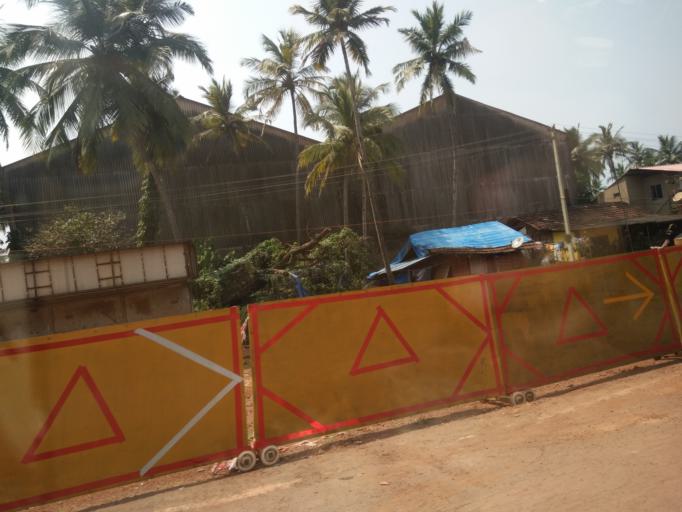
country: IN
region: Goa
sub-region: South Goa
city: Cortalim
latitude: 15.3982
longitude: 73.9104
